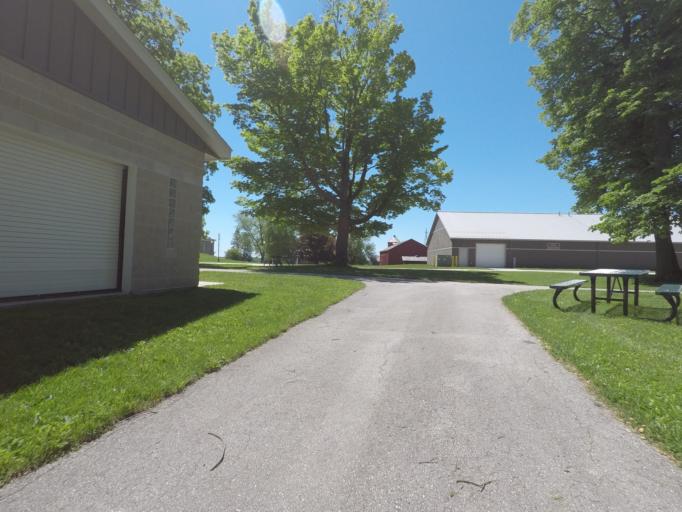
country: US
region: Wisconsin
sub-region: Sheboygan County
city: Sheboygan
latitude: 43.7540
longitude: -87.7487
